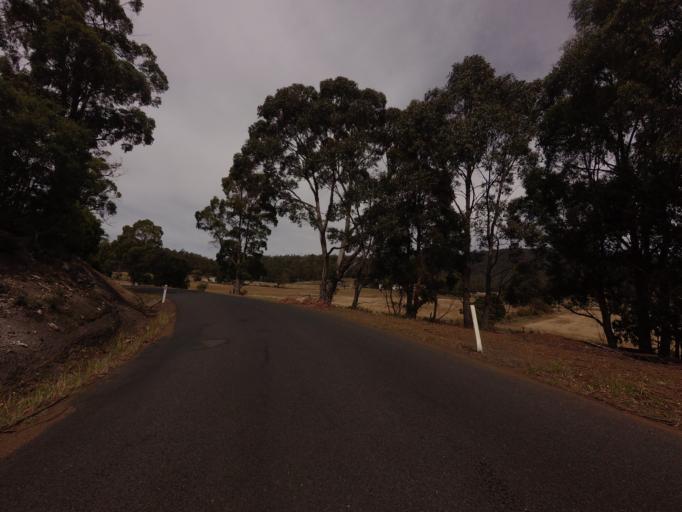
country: AU
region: Tasmania
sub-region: Sorell
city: Sorell
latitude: -42.5764
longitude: 147.5583
